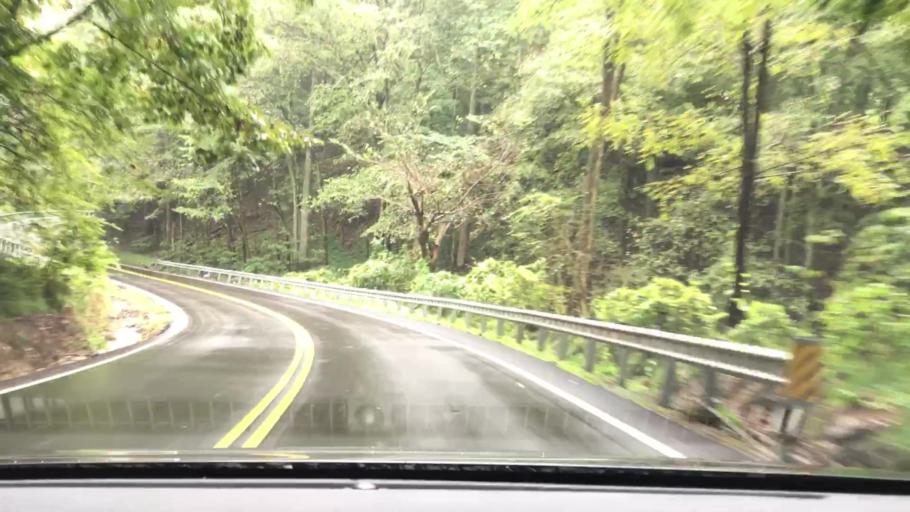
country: US
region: Tennessee
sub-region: Macon County
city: Red Boiling Springs
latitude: 36.4619
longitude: -85.8822
